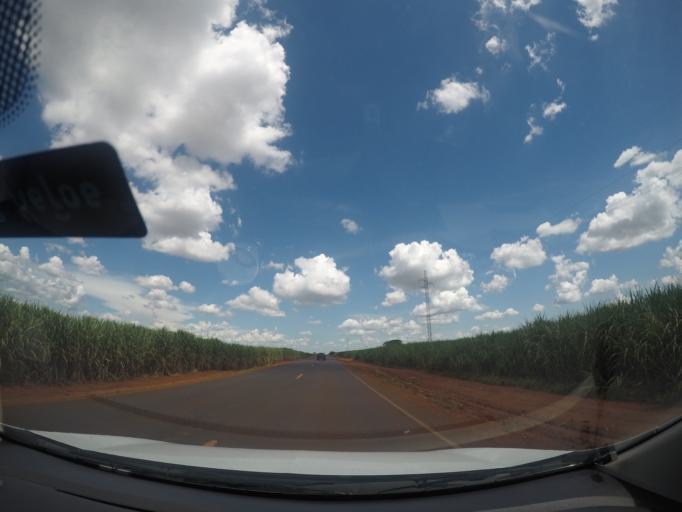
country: BR
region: Minas Gerais
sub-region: Frutal
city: Frutal
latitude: -19.8558
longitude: -48.7339
